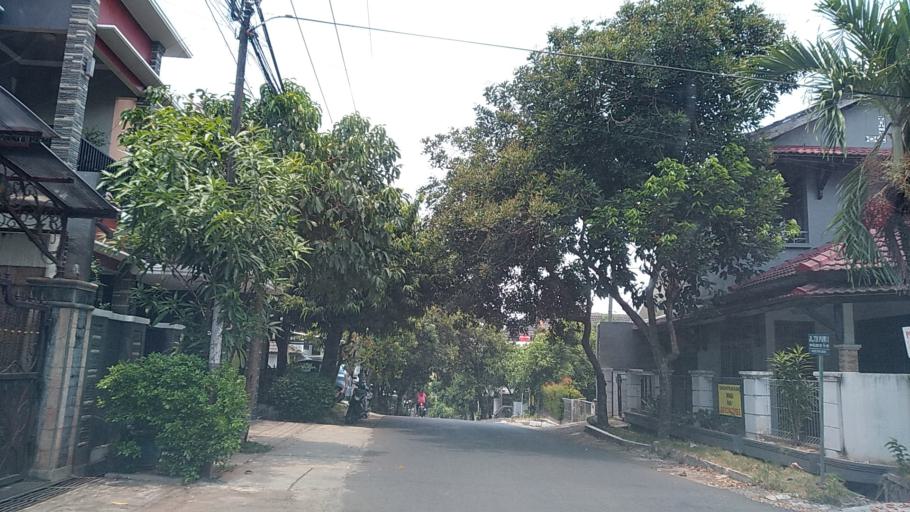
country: ID
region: Central Java
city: Ungaran
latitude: -7.0756
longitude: 110.4271
